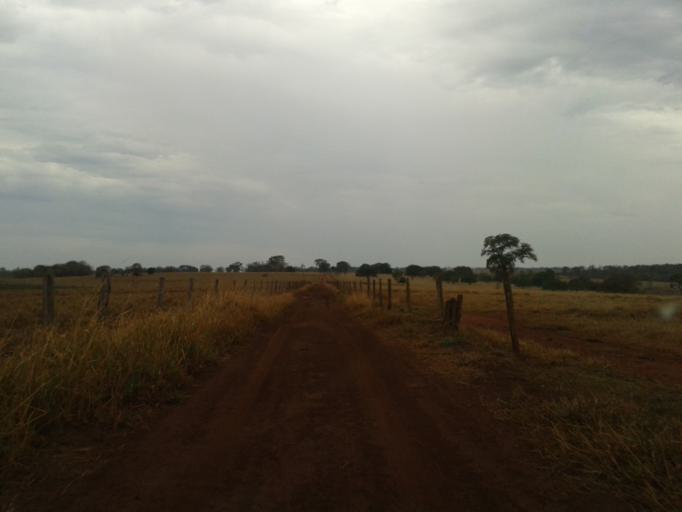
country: BR
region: Minas Gerais
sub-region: Santa Vitoria
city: Santa Vitoria
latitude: -18.8675
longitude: -49.8233
